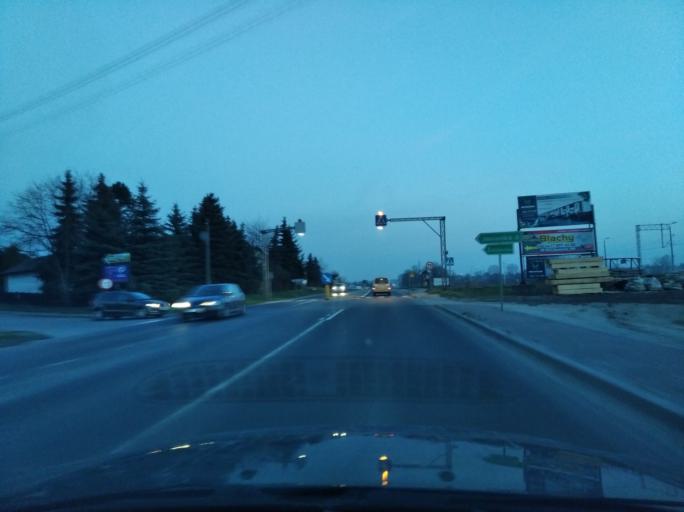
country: PL
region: Subcarpathian Voivodeship
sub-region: Powiat rzeszowski
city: Rudna Mala
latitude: 50.0961
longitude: 21.9798
